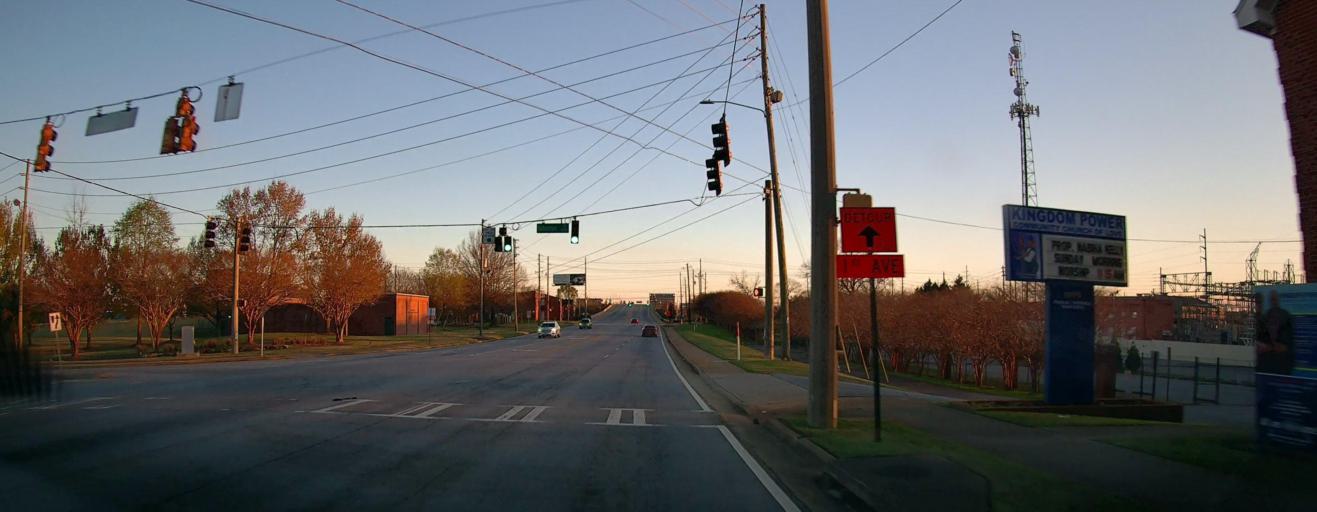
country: US
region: Alabama
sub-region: Russell County
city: Phenix City
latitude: 32.4815
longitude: -84.9903
